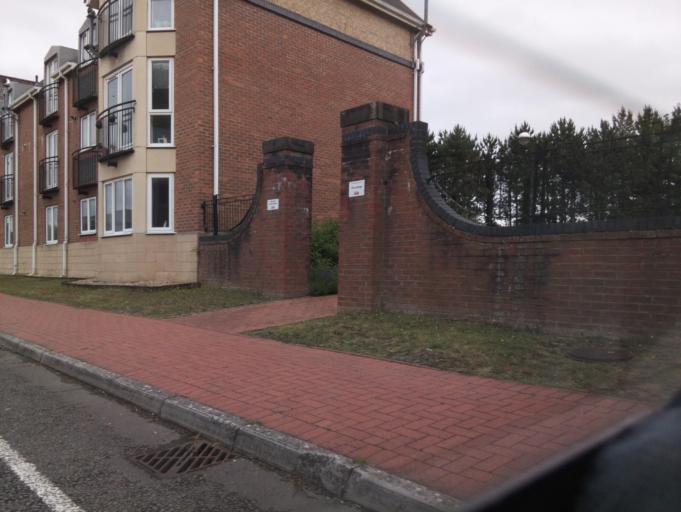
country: GB
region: Wales
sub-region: Vale of Glamorgan
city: Penarth
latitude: 51.4451
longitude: -3.1830
